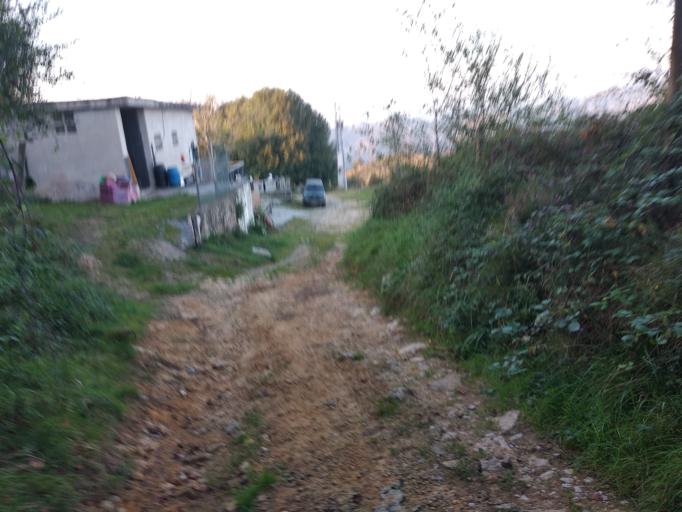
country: ES
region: Cantabria
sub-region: Provincia de Cantabria
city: Entrambasaguas
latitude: 43.3255
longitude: -3.6774
